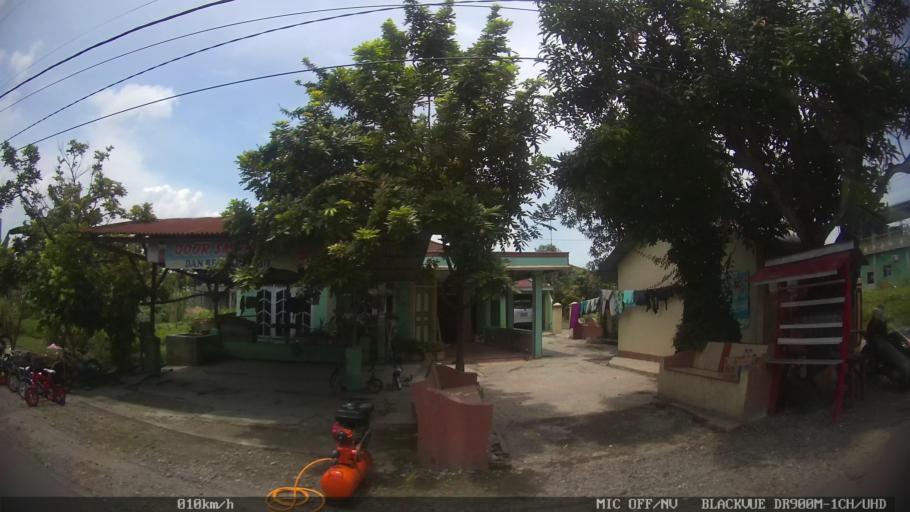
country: ID
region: North Sumatra
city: Labuhan Deli
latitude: 3.7089
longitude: 98.6755
